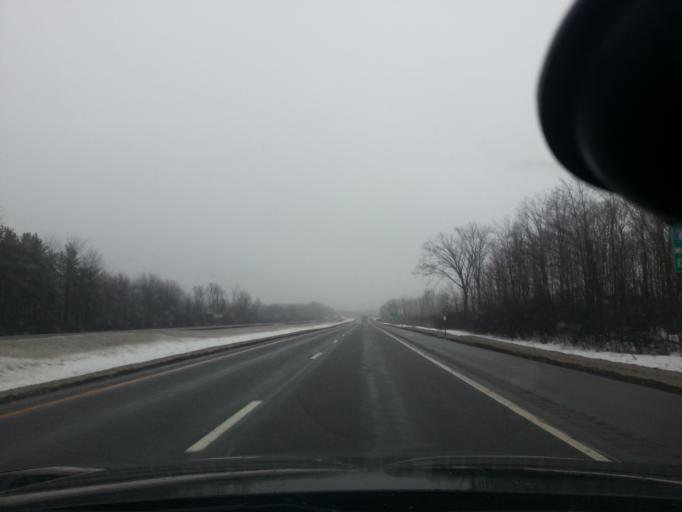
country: US
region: New York
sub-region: Oswego County
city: Pulaski
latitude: 43.6380
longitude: -76.0813
